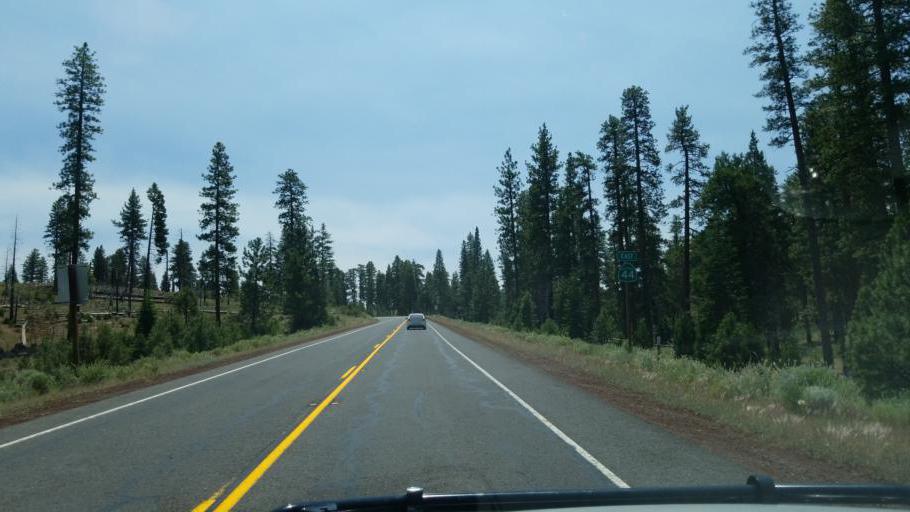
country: US
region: California
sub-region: Shasta County
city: Burney
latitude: 40.6996
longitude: -121.3933
